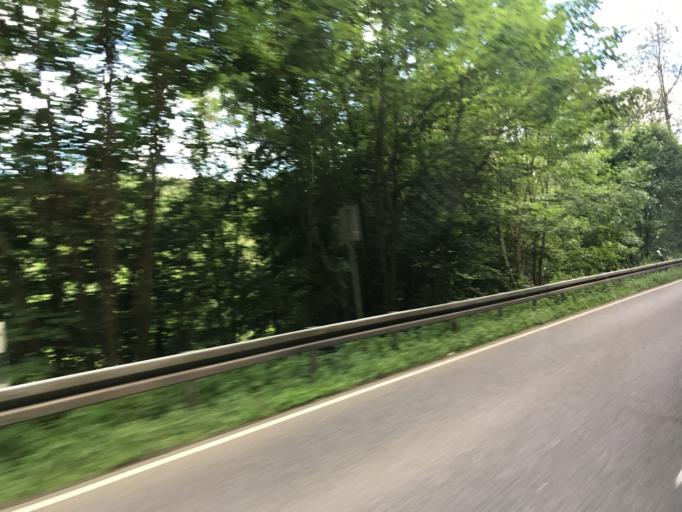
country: DE
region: Hesse
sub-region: Regierungsbezirk Darmstadt
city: Schlangenbad
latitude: 50.0736
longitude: 8.1092
